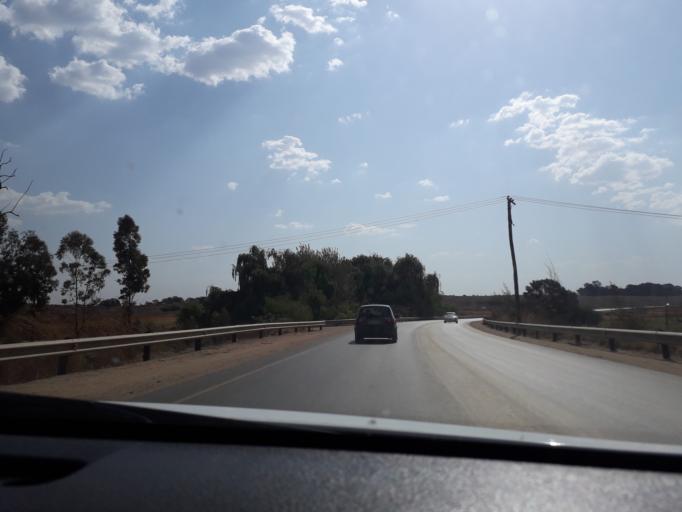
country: ZA
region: Gauteng
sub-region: Ekurhuleni Metropolitan Municipality
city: Tembisa
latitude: -26.0519
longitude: 28.2668
